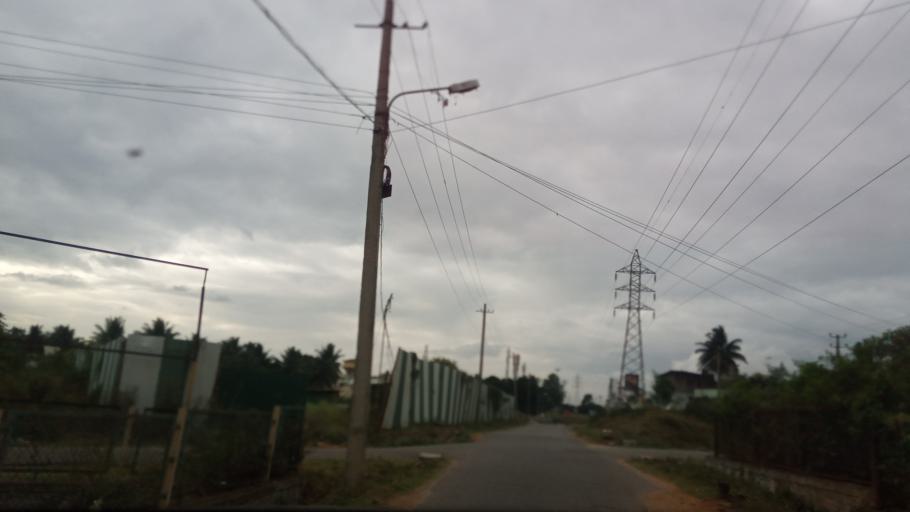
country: IN
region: Karnataka
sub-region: Mysore
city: Mysore
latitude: 12.2933
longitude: 76.6163
